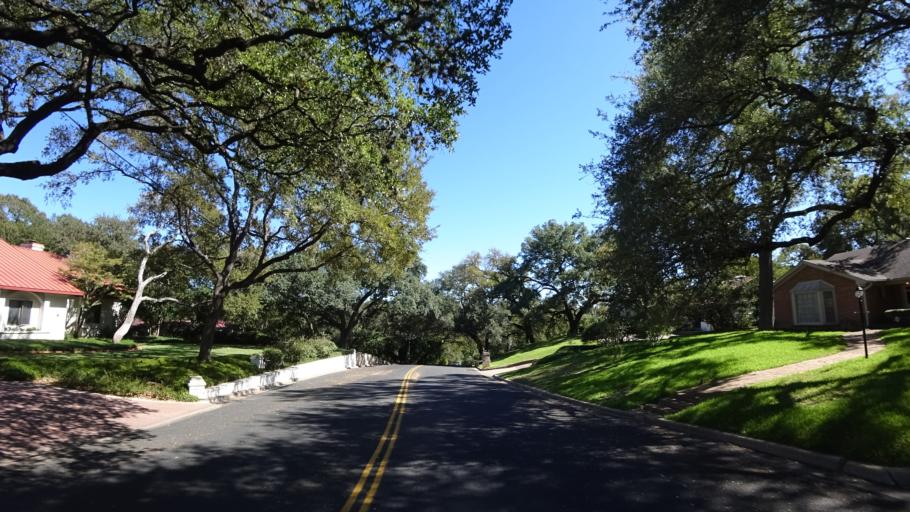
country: US
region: Texas
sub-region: Travis County
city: West Lake Hills
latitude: 30.3195
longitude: -97.7671
